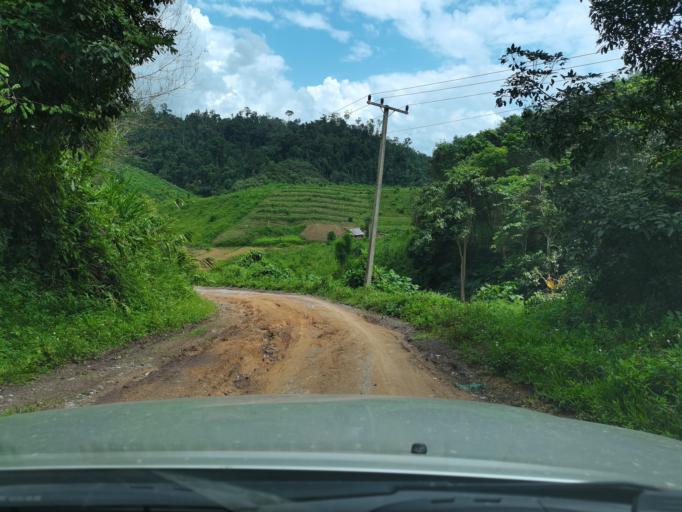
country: LA
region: Loungnamtha
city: Muang Long
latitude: 20.7016
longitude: 101.0163
